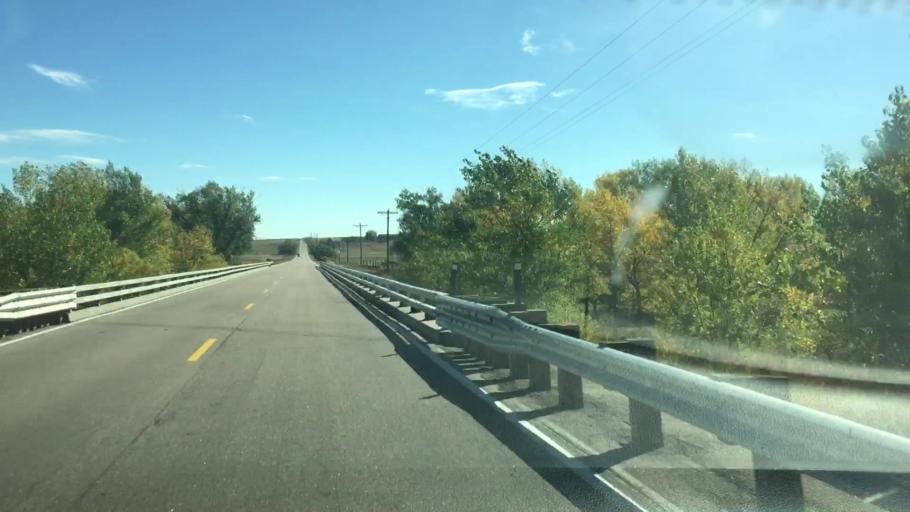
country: US
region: Colorado
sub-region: Elbert County
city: Kiowa
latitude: 39.2736
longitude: -104.1431
